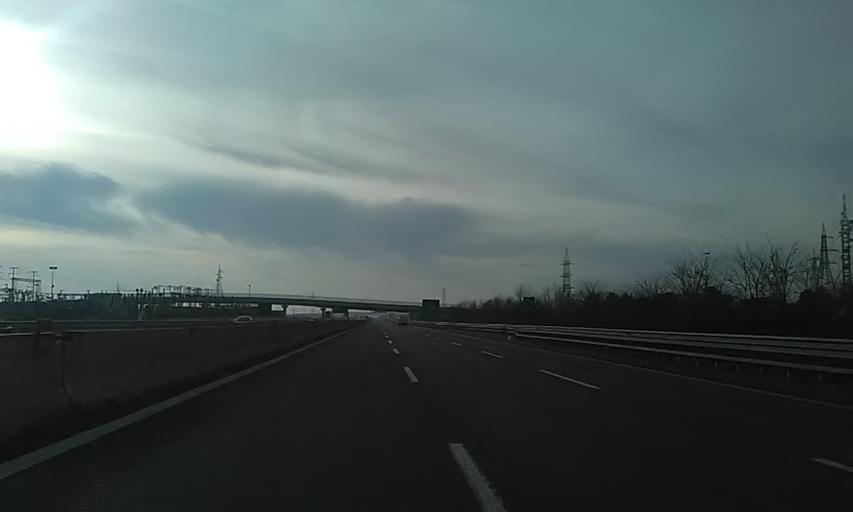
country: IT
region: Piedmont
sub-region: Provincia di Torino
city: Rondissone
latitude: 45.2312
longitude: 7.9419
